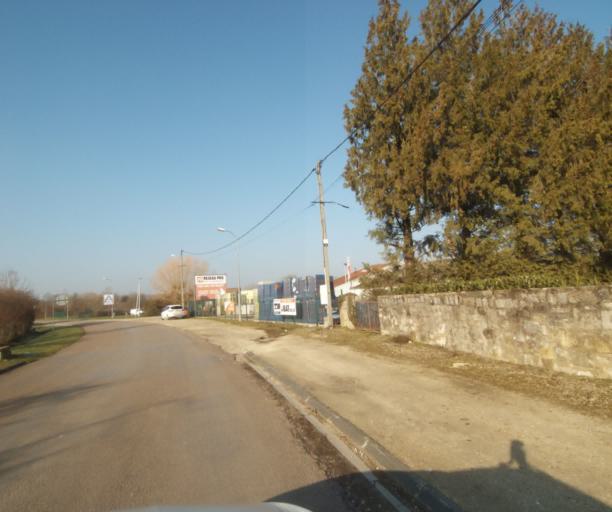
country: FR
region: Champagne-Ardenne
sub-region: Departement de la Haute-Marne
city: Wassy
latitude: 48.5005
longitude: 4.9382
